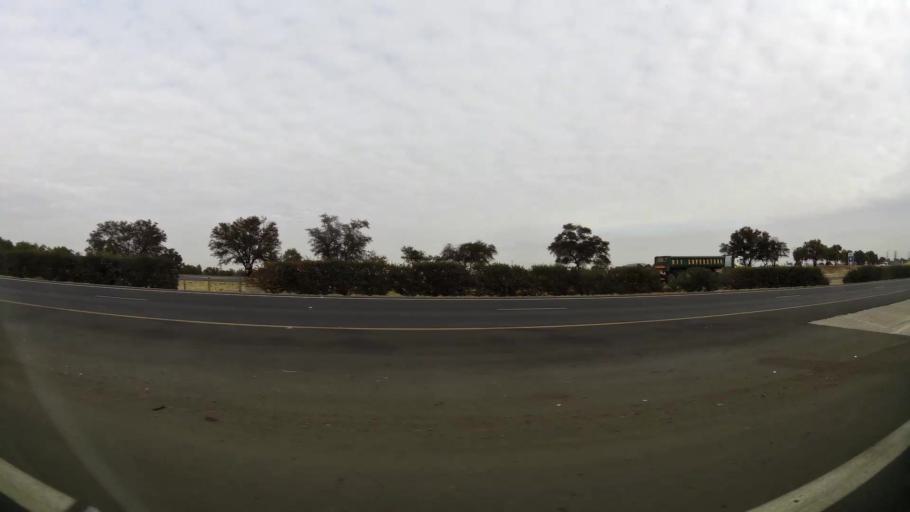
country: ZA
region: Orange Free State
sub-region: Mangaung Metropolitan Municipality
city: Bloemfontein
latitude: -29.1302
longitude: 26.1646
